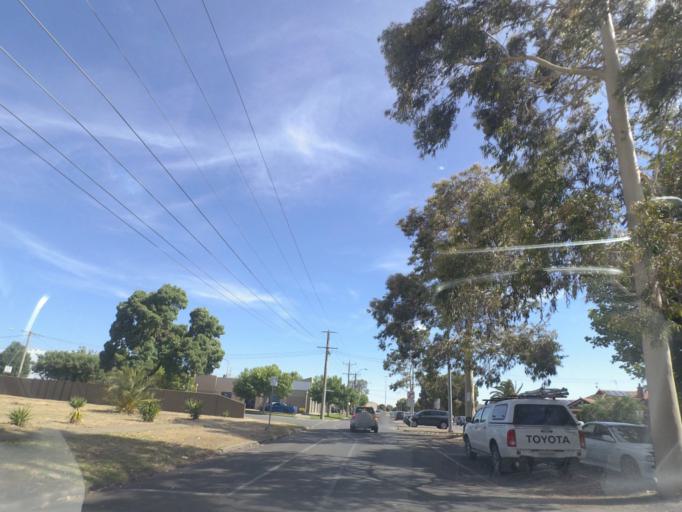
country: AU
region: Victoria
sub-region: Greater Shepparton
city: Shepparton
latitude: -36.3843
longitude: 145.4028
